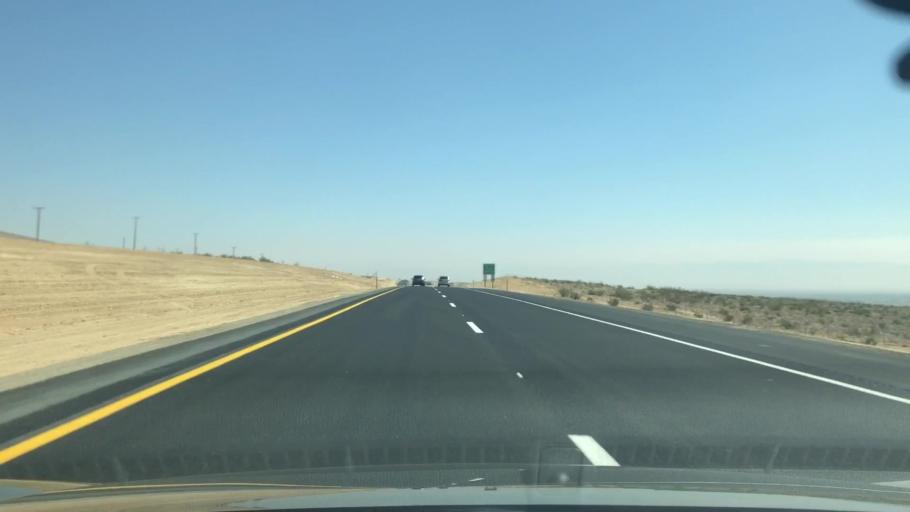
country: US
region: California
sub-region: Kern County
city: Inyokern
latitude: 35.6290
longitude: -117.8885
